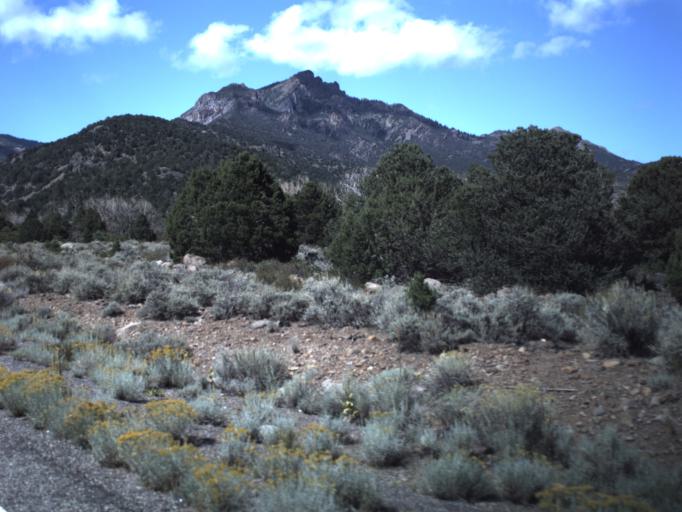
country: US
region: Utah
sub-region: Piute County
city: Junction
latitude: 38.2639
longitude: -112.3005
